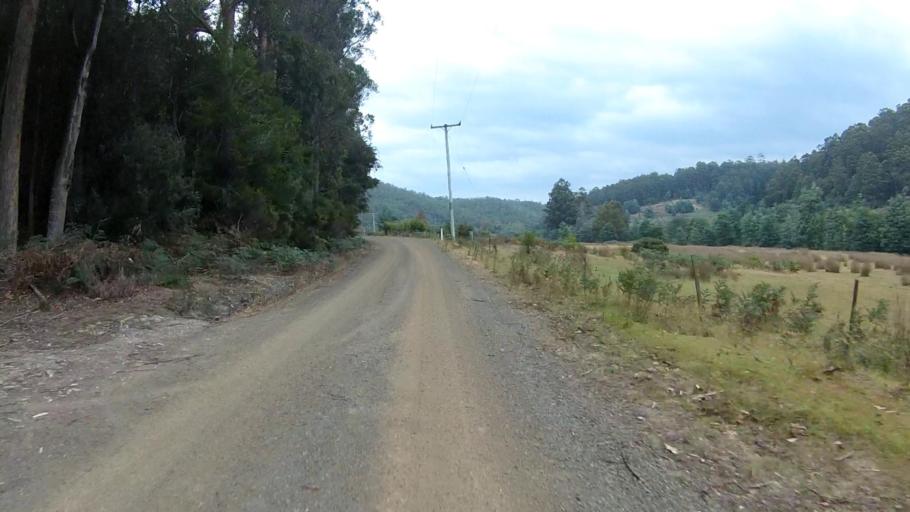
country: AU
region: Tasmania
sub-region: Kingborough
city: Kettering
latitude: -43.2152
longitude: 147.1773
